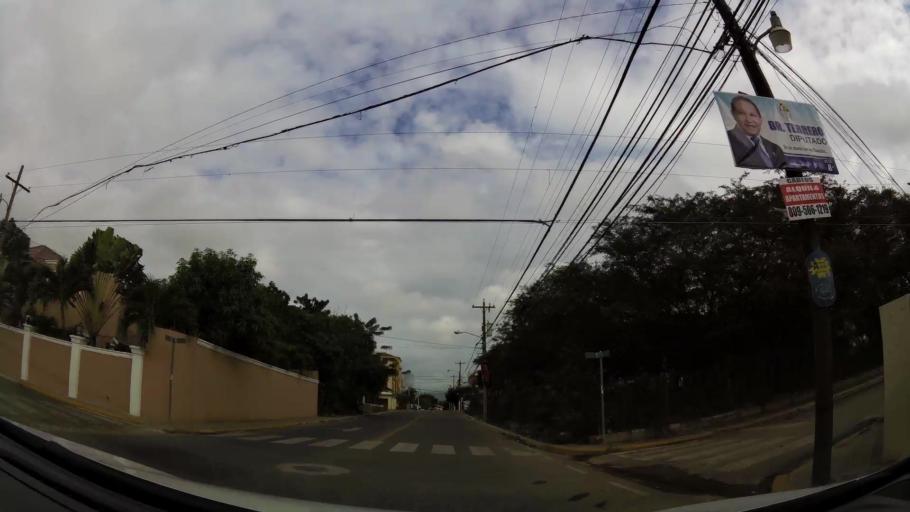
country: DO
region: Santiago
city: Santiago de los Caballeros
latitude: 19.4640
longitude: -70.6573
